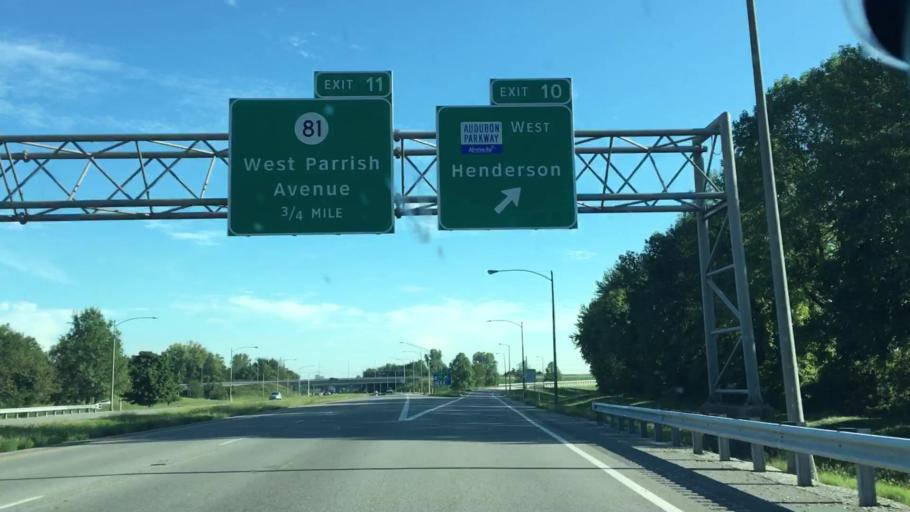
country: US
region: Kentucky
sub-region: Daviess County
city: Owensboro
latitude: 37.7695
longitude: -87.1649
